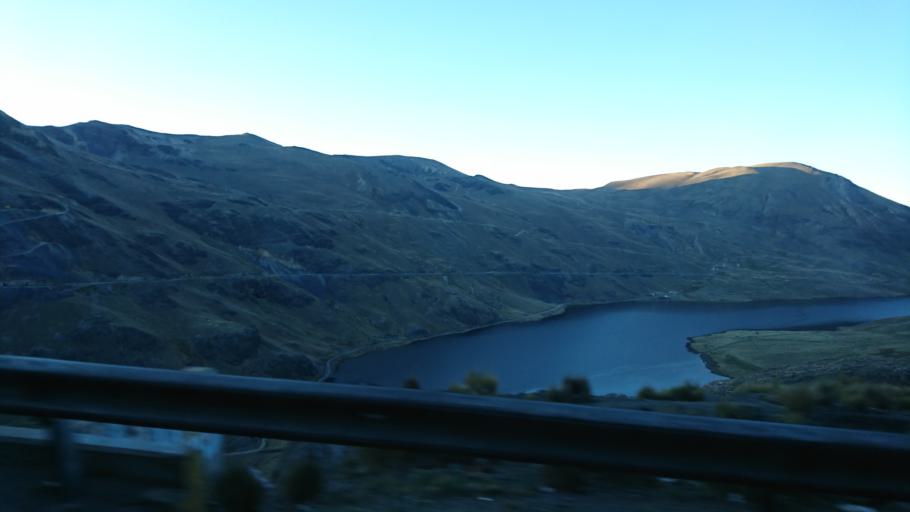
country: BO
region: La Paz
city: La Paz
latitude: -16.3847
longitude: -68.0417
